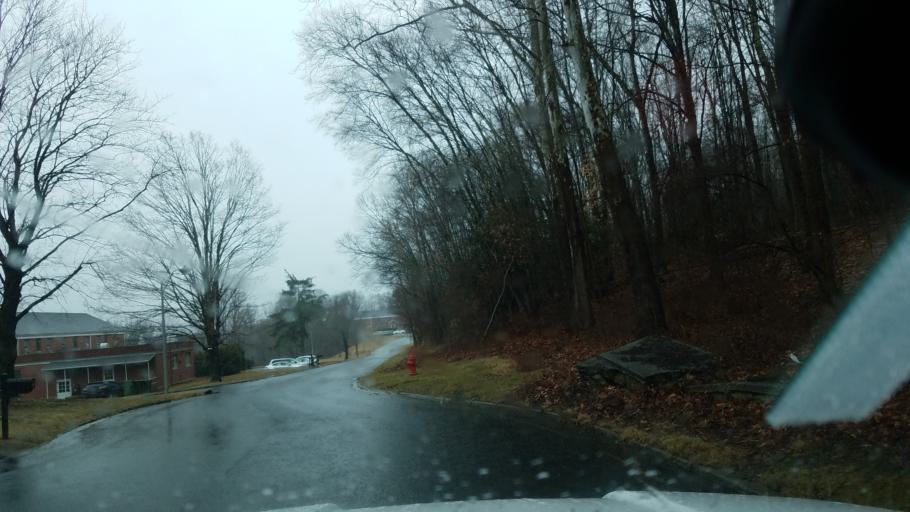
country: US
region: Connecticut
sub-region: New Haven County
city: Heritage Village
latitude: 41.4883
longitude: -73.2634
